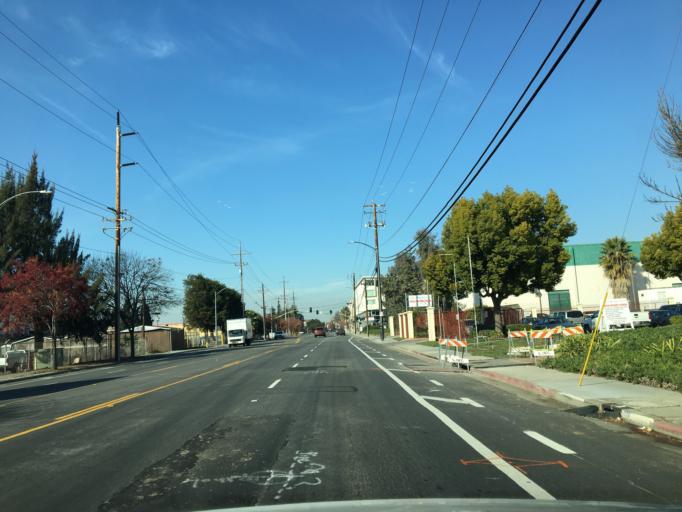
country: US
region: California
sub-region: Santa Clara County
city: San Jose
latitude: 37.3635
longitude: -121.8660
